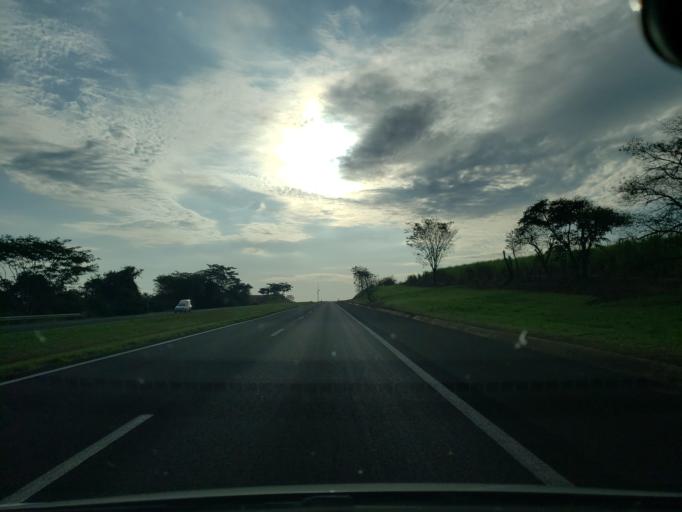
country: BR
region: Sao Paulo
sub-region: Mirandopolis
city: Mirandopolis
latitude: -21.1111
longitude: -51.0233
